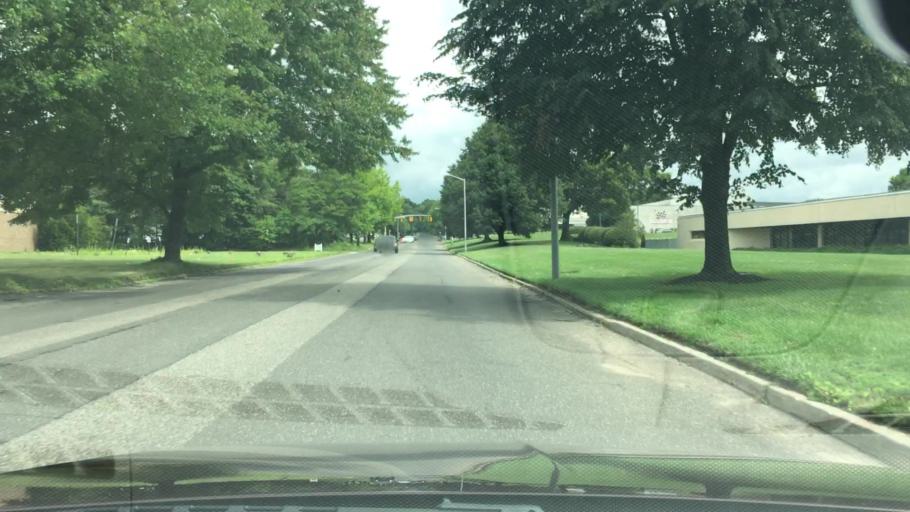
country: US
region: New York
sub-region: Suffolk County
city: Commack
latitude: 40.8116
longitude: -73.2705
